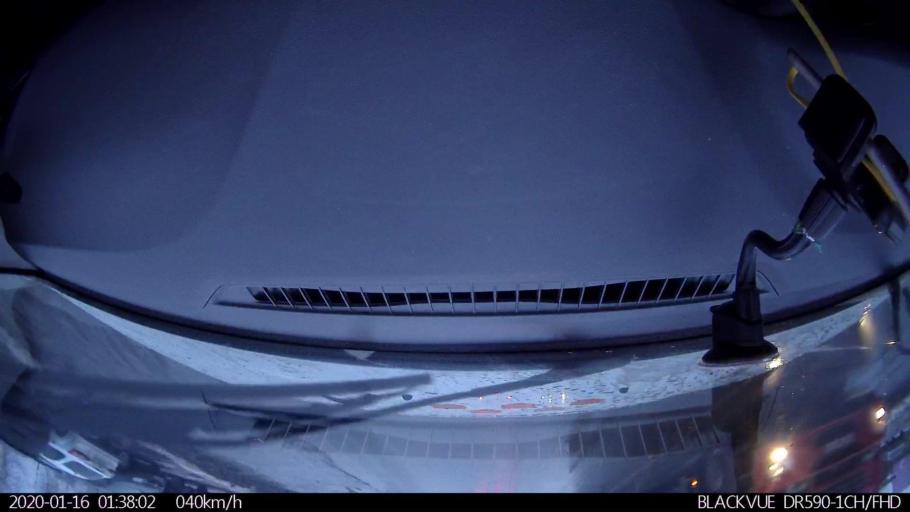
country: RU
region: Nizjnij Novgorod
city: Gorbatovka
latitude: 56.3389
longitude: 43.8039
